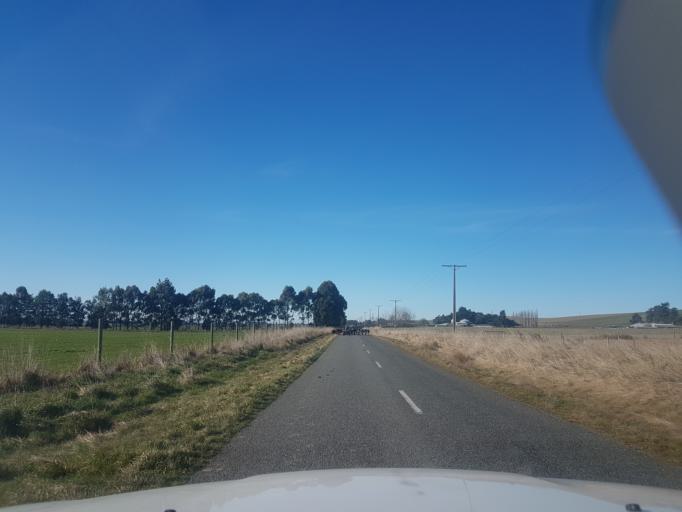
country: NZ
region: Canterbury
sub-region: Timaru District
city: Pleasant Point
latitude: -44.2912
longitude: 171.0615
